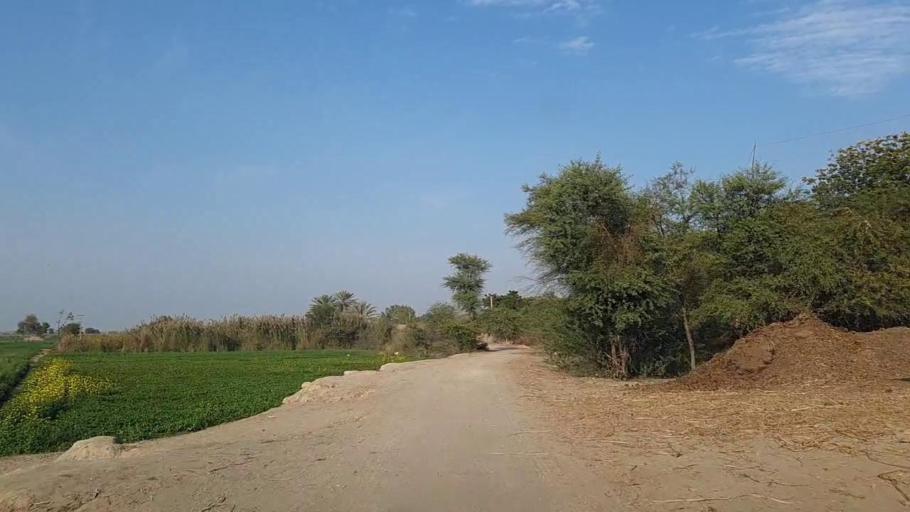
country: PK
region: Sindh
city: Nawabshah
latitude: 26.3727
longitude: 68.4944
